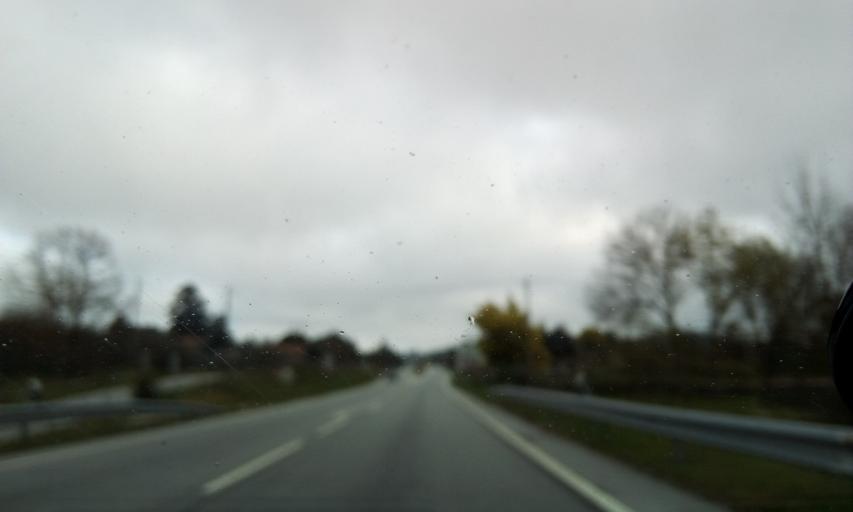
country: PT
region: Guarda
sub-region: Fornos de Algodres
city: Fornos de Algodres
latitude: 40.6351
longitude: -7.4992
